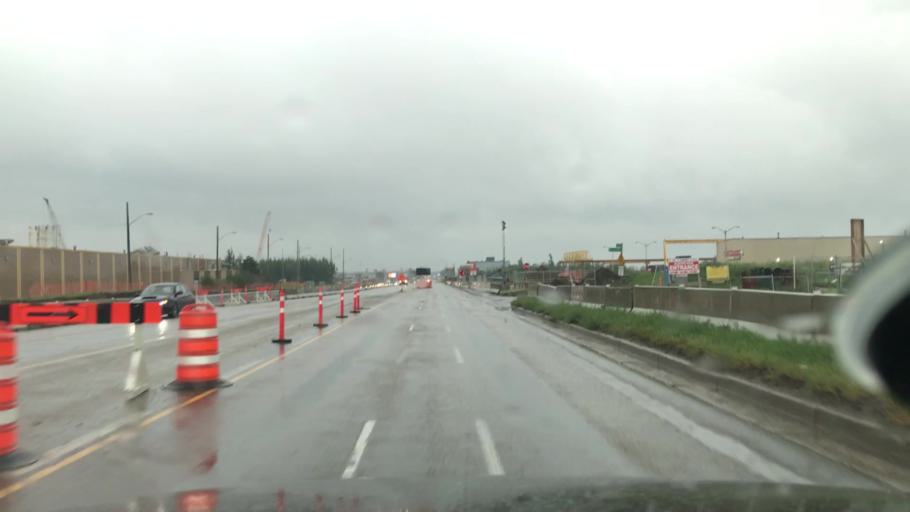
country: CA
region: Alberta
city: Edmonton
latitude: 53.4944
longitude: -113.4426
